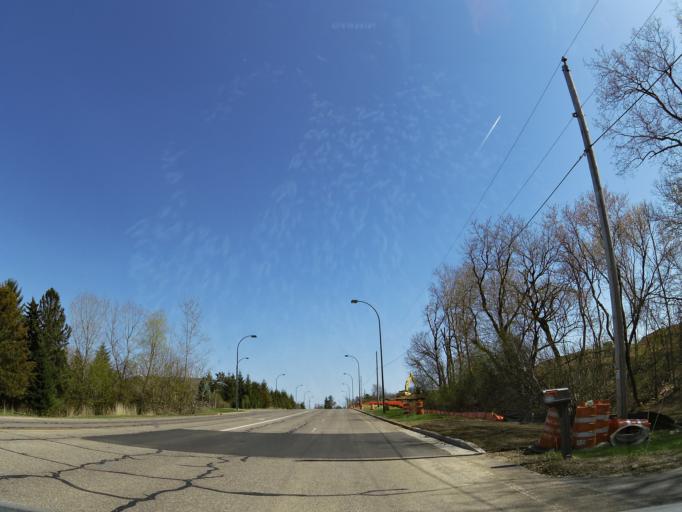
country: US
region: Wisconsin
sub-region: Saint Croix County
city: Hudson
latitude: 44.9611
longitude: -92.7059
